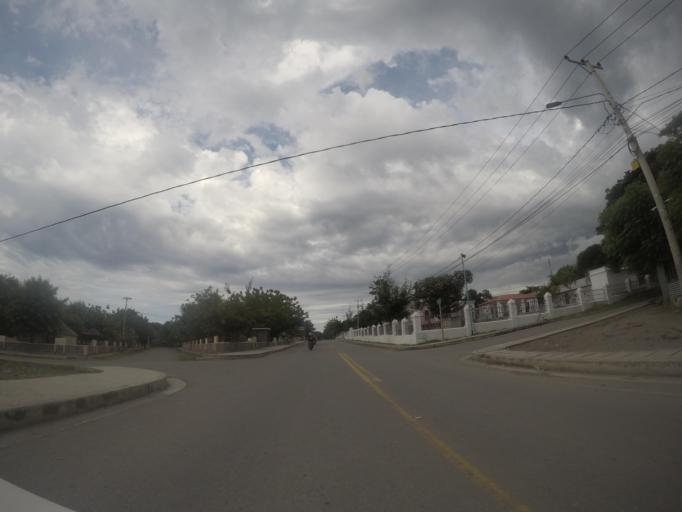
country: TL
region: Liquica
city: Liquica
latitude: -8.5939
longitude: 125.3268
